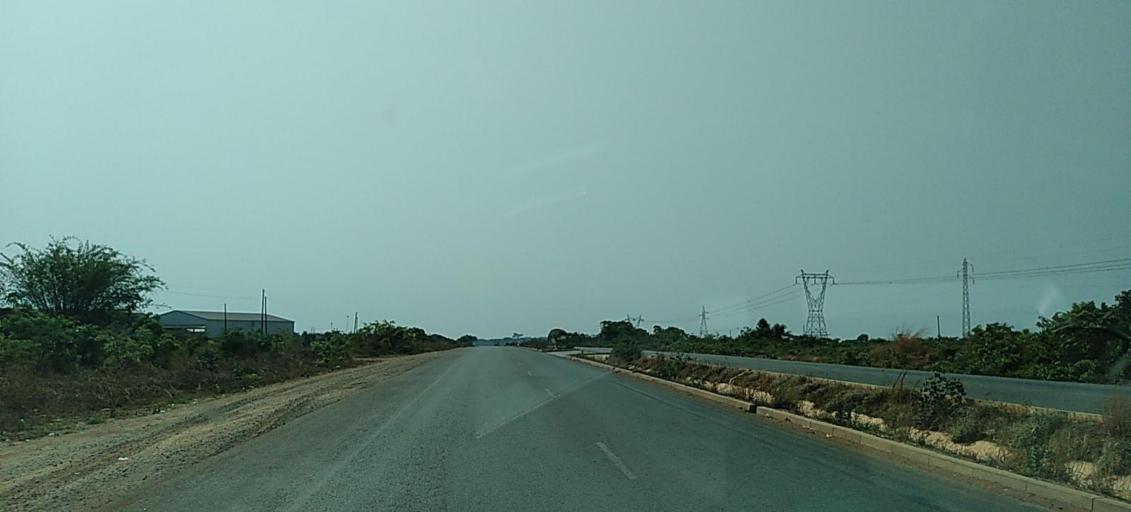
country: ZM
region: Copperbelt
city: Chingola
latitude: -12.5706
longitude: 27.9091
